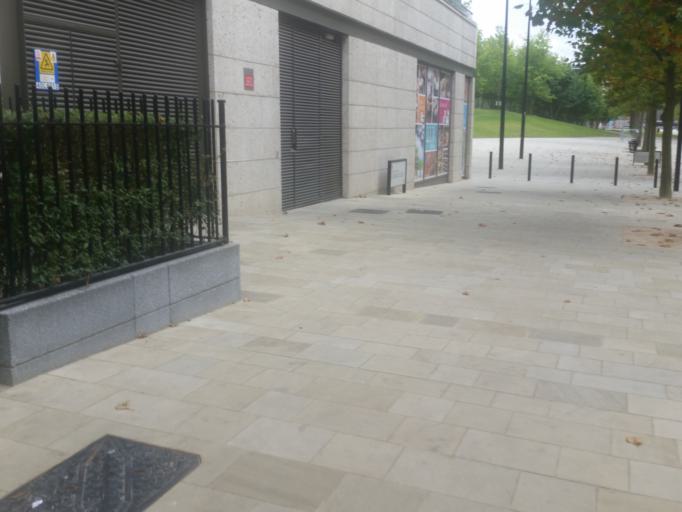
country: GB
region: England
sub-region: Greater London
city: Poplar
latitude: 51.5477
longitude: -0.0113
